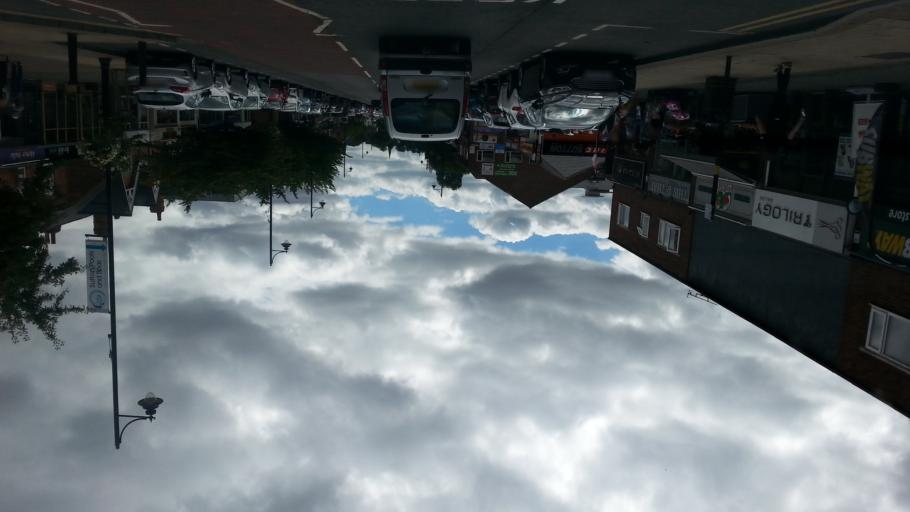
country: GB
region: England
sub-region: City and Borough of Birmingham
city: Sutton Coldfield
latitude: 52.5494
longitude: -1.8414
